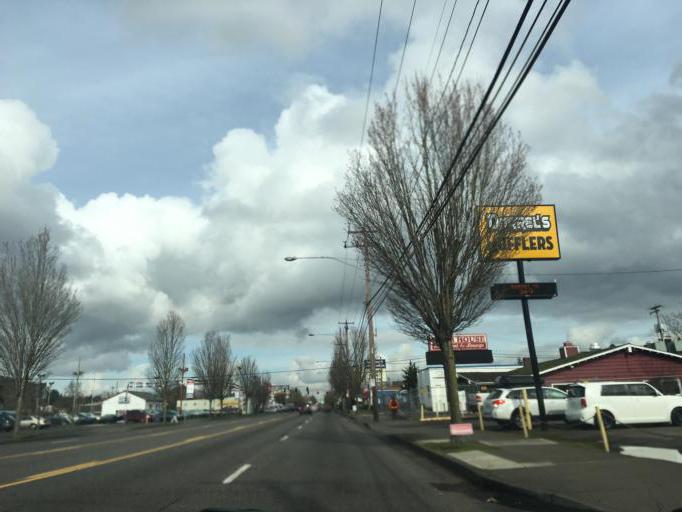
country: US
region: Oregon
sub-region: Multnomah County
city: Lents
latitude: 45.4955
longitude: -122.5787
